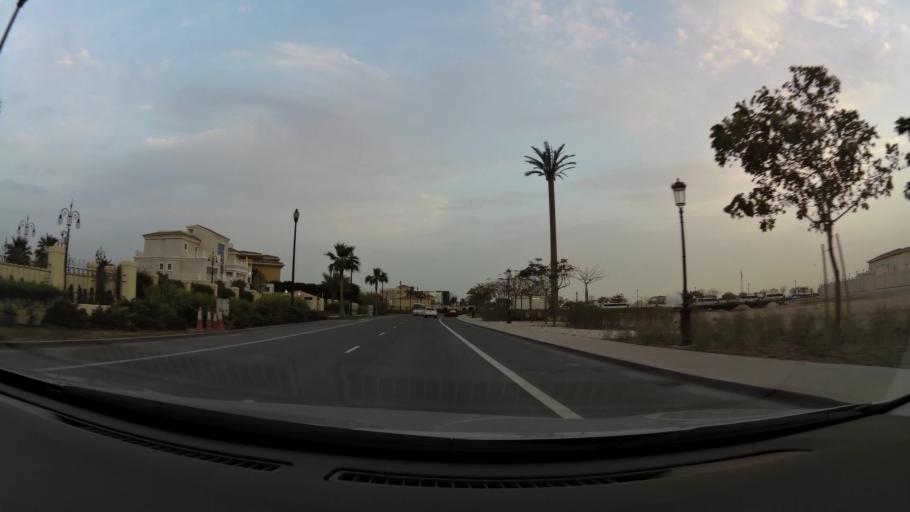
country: QA
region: Baladiyat ad Dawhah
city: Doha
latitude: 25.3676
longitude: 51.5631
